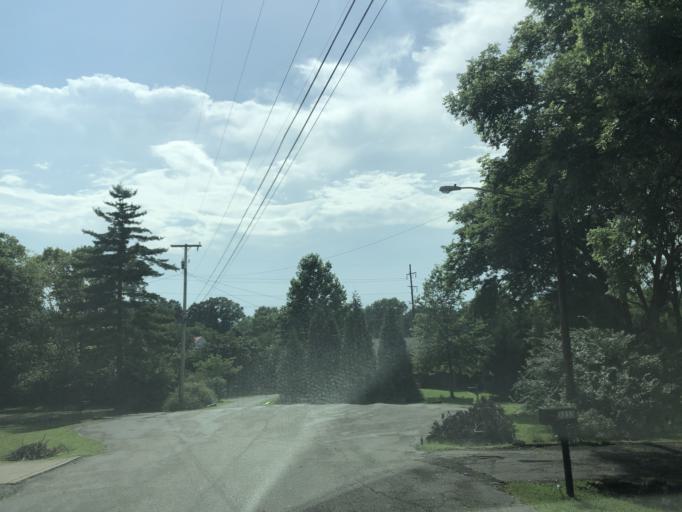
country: US
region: Tennessee
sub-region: Davidson County
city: Lakewood
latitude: 36.1737
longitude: -86.6724
